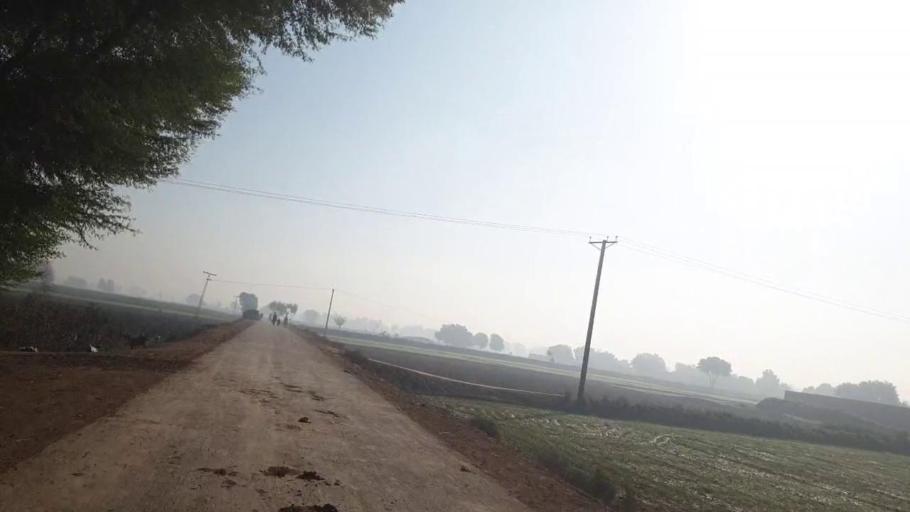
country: PK
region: Sindh
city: Dadu
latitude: 26.6751
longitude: 67.7932
